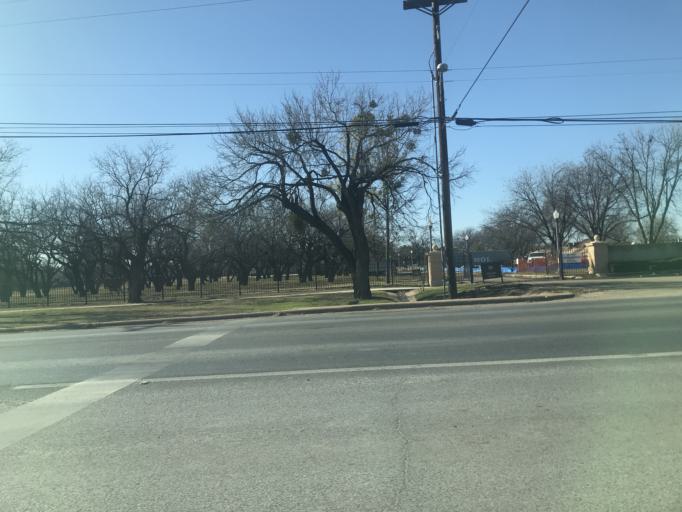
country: US
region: Texas
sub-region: Taylor County
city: Abilene
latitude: 32.4158
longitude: -99.7424
